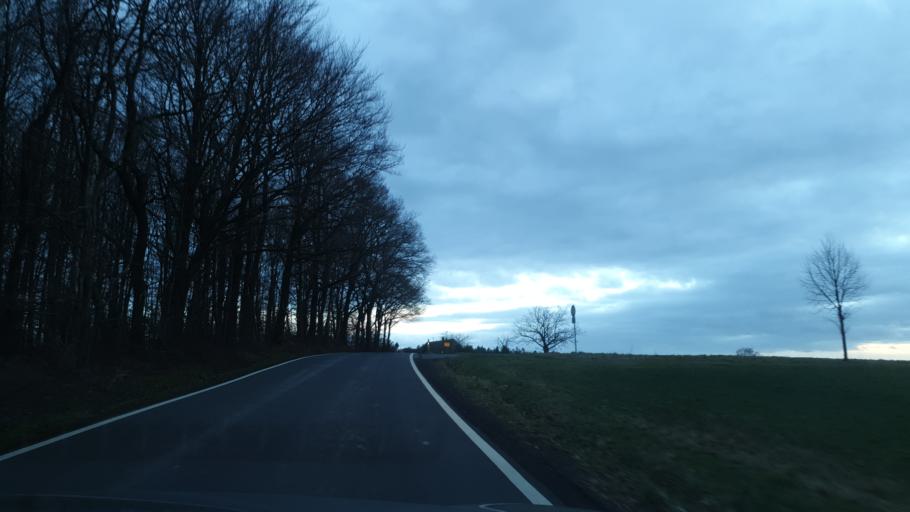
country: DE
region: Rheinland-Pfalz
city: Ratzert
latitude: 50.6498
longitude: 7.6327
